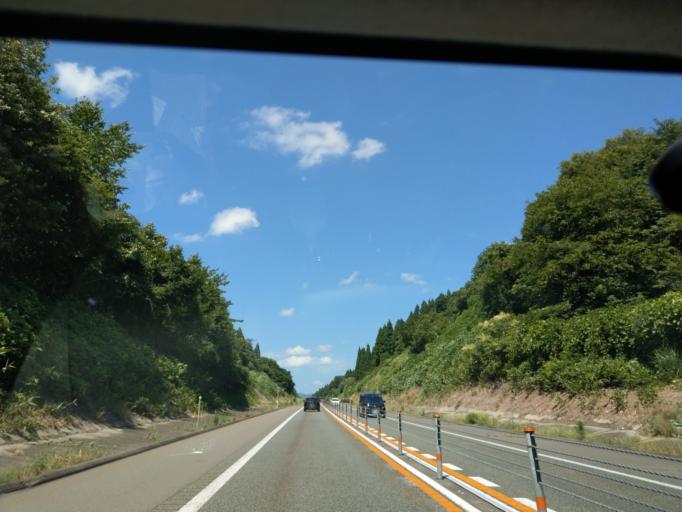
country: JP
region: Akita
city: Akita
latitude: 39.6804
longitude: 140.1856
